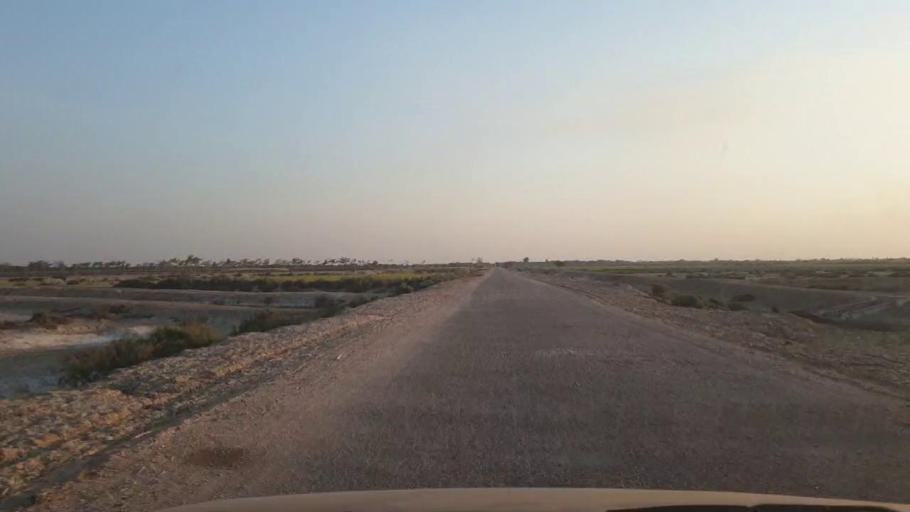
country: PK
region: Sindh
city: Mirwah Gorchani
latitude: 25.2773
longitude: 68.9394
